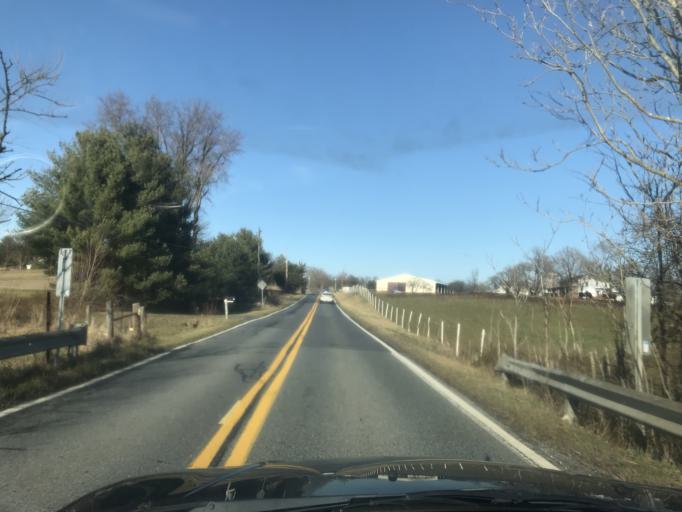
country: US
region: Maryland
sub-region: Montgomery County
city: Damascus
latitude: 39.3258
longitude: -77.2265
